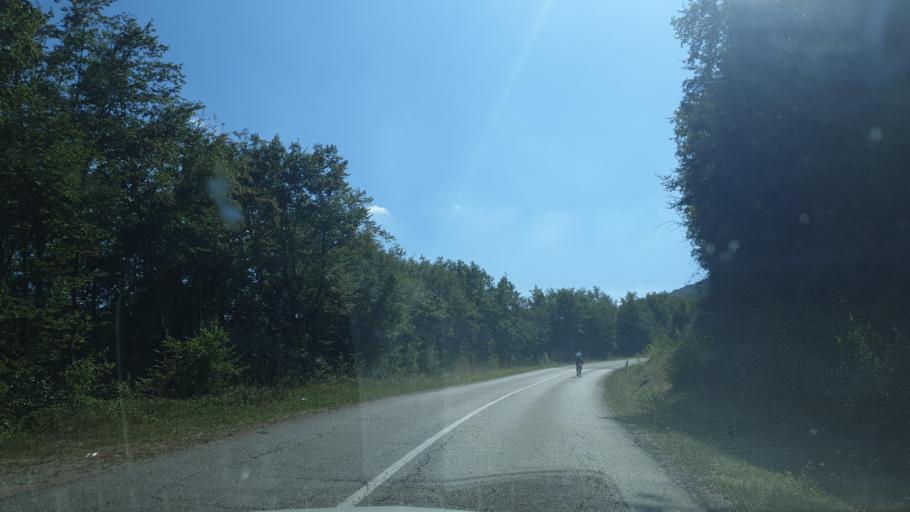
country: RS
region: Central Serbia
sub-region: Kolubarski Okrug
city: Mionica
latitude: 44.1486
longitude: 20.0210
